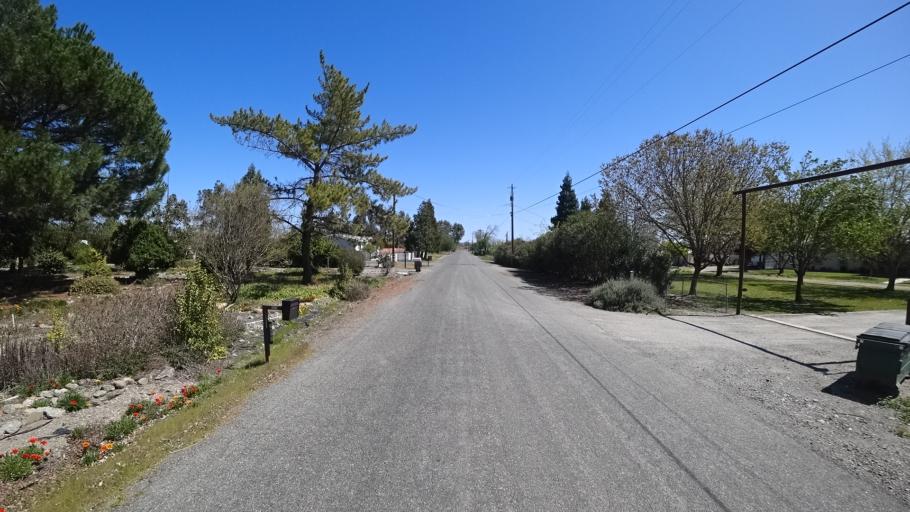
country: US
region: California
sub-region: Glenn County
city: Orland
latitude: 39.7769
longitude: -122.2336
